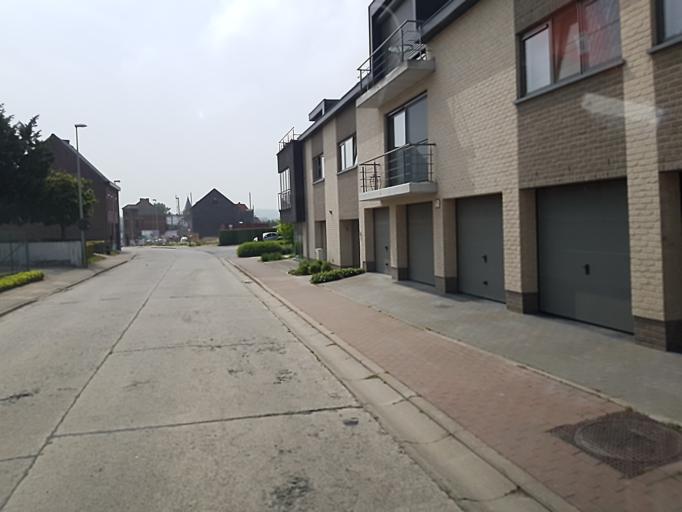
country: BE
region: Flanders
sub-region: Provincie Oost-Vlaanderen
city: Geraardsbergen
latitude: 50.7995
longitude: 3.8983
